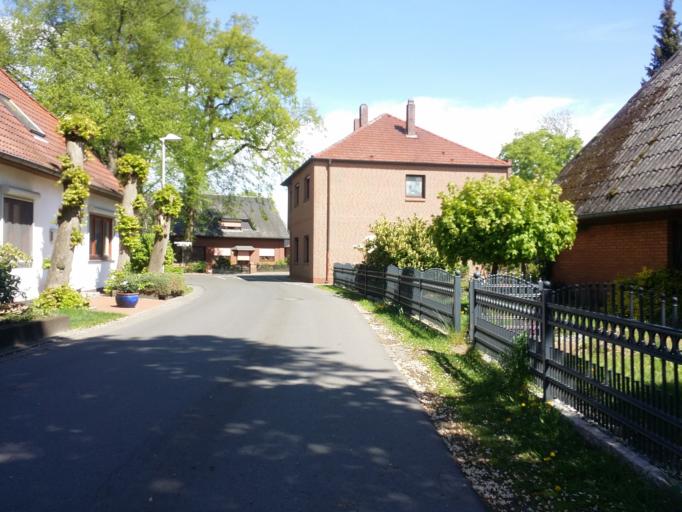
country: DE
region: Lower Saxony
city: Delmenhorst
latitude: 53.0751
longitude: 8.6594
